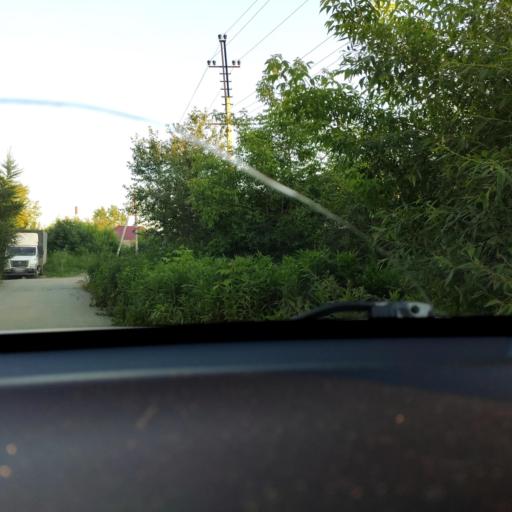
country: RU
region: Tatarstan
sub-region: Gorod Kazan'
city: Kazan
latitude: 55.8608
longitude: 49.0623
